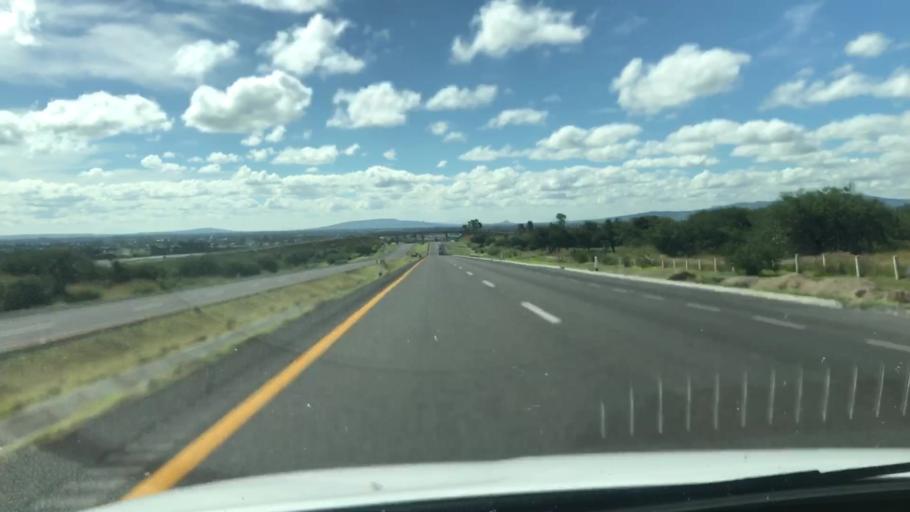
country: MX
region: Guanajuato
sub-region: Silao de la Victoria
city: Bajio de Bonillas
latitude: 20.9395
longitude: -101.5028
